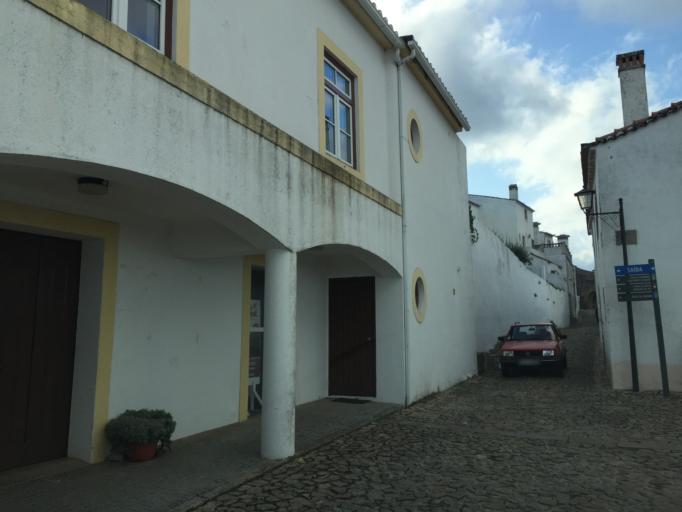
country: PT
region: Portalegre
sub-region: Marvao
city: Marvao
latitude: 39.3948
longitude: -7.3764
